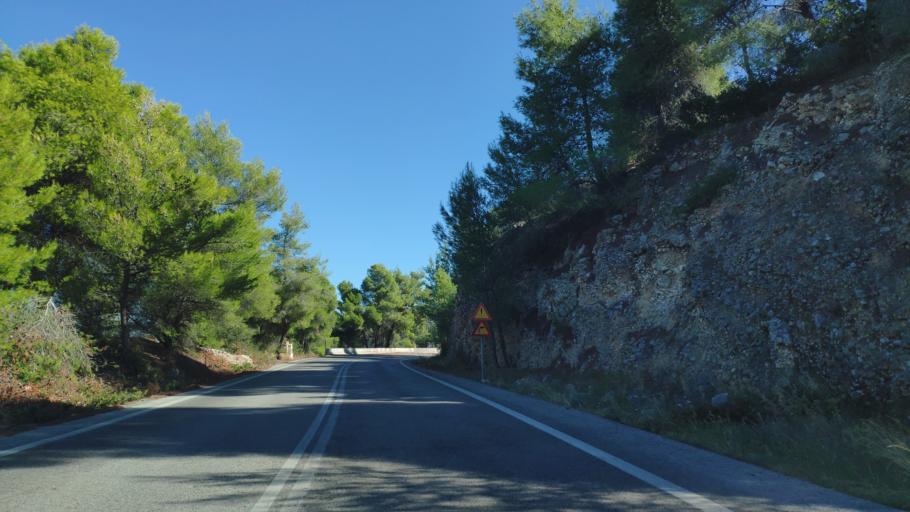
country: GR
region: Peloponnese
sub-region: Nomos Korinthias
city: Sofikon
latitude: 37.8275
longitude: 23.0633
